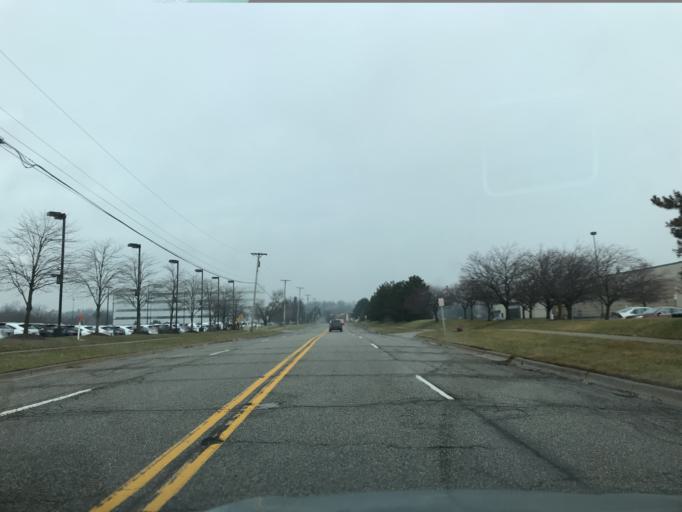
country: US
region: Michigan
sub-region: Oakland County
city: Franklin
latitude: 42.4971
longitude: -83.2959
